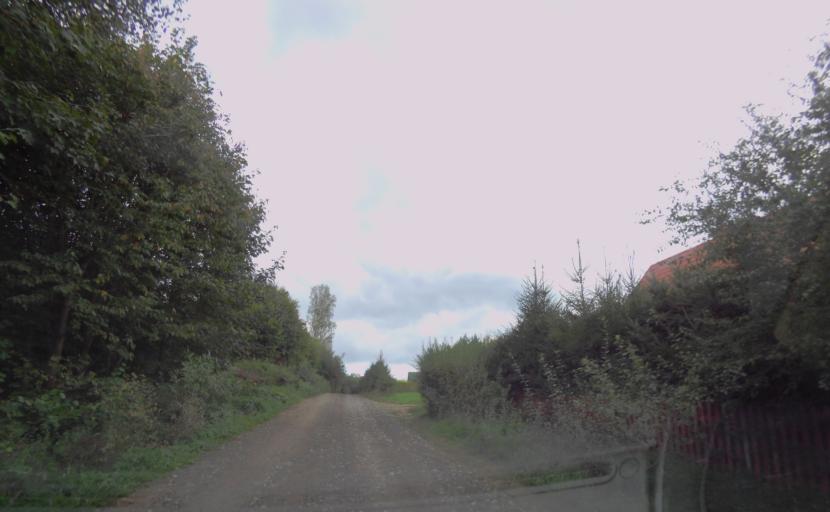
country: PL
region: Subcarpathian Voivodeship
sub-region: Powiat leski
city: Polanczyk
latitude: 49.3143
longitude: 22.5073
